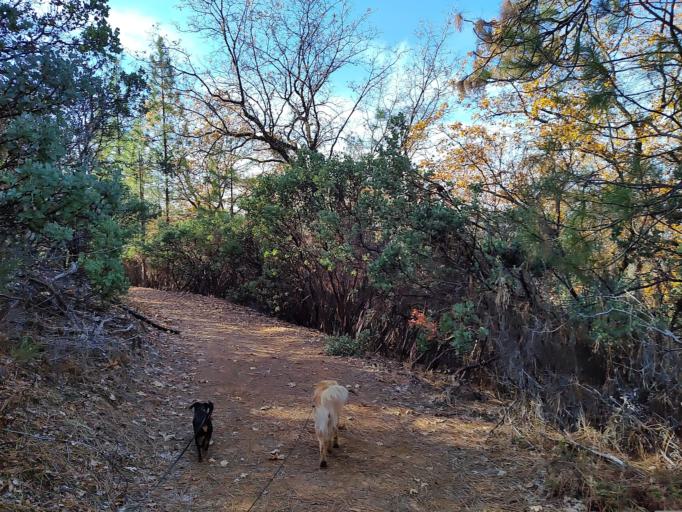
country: US
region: California
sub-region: Placer County
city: Meadow Vista
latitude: 39.0263
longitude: -120.9854
